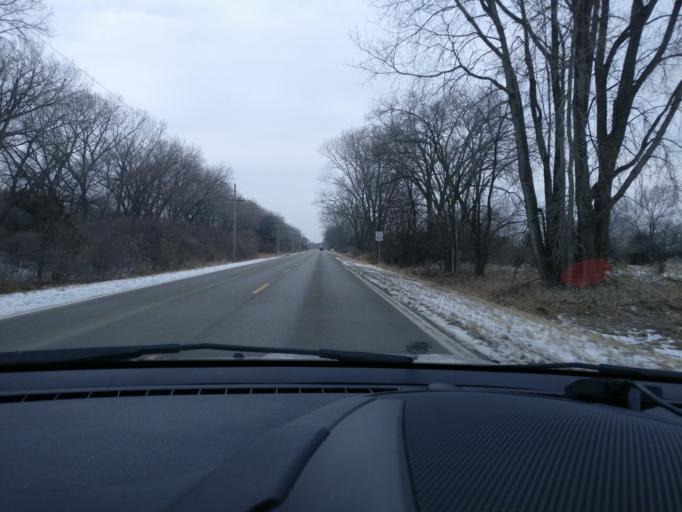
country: US
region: Nebraska
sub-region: Dodge County
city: Fremont
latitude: 41.4433
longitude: -96.5378
